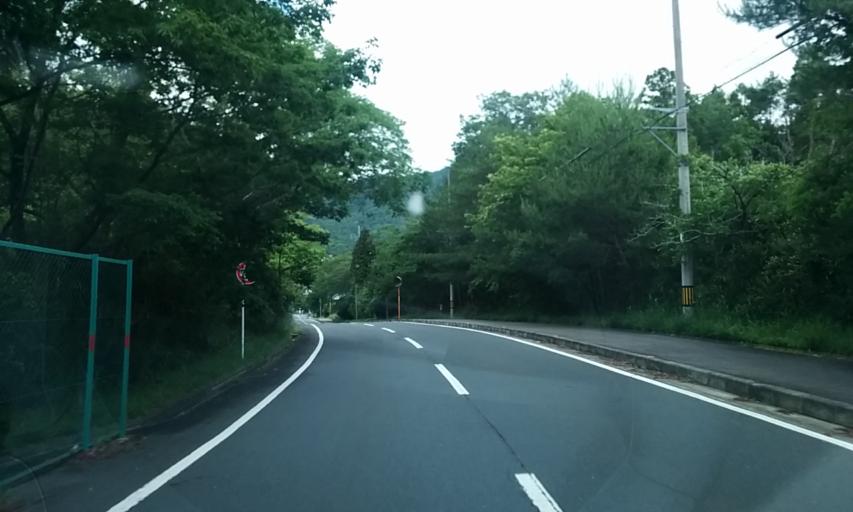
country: JP
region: Kyoto
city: Kameoka
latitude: 35.0128
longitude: 135.4349
